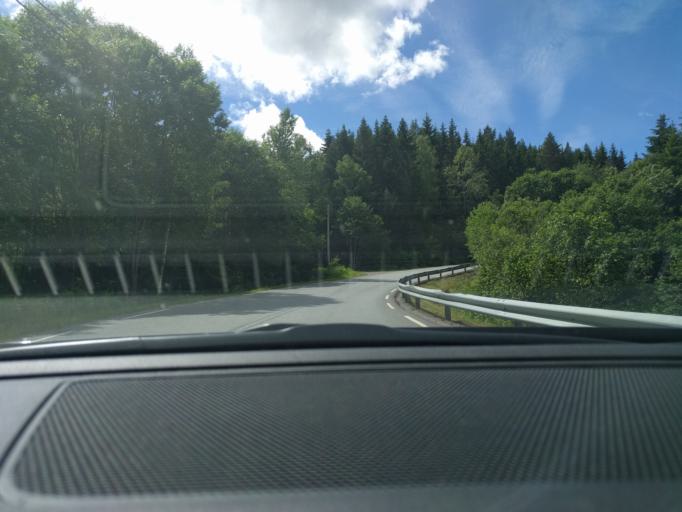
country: NO
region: Vestfold
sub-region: Lardal
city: Svarstad
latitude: 59.4084
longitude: 9.9291
